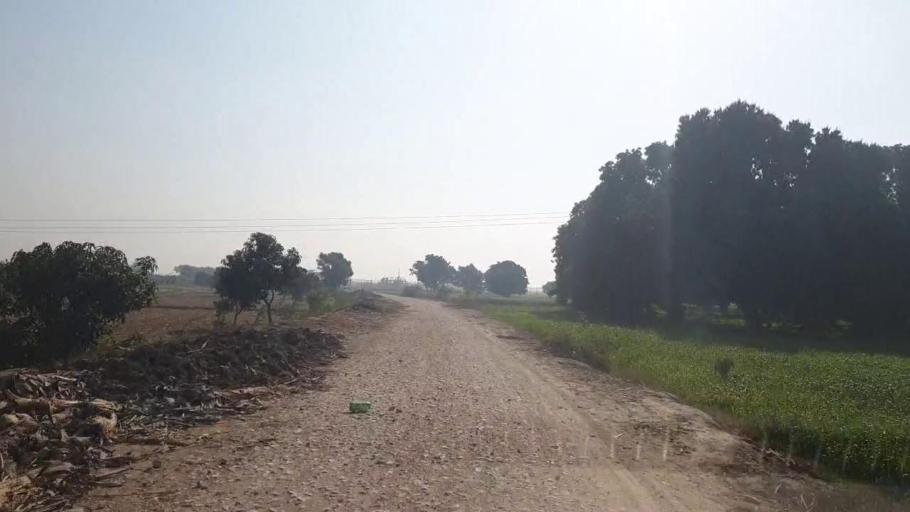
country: PK
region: Sindh
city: Tando Allahyar
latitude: 25.5471
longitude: 68.7482
